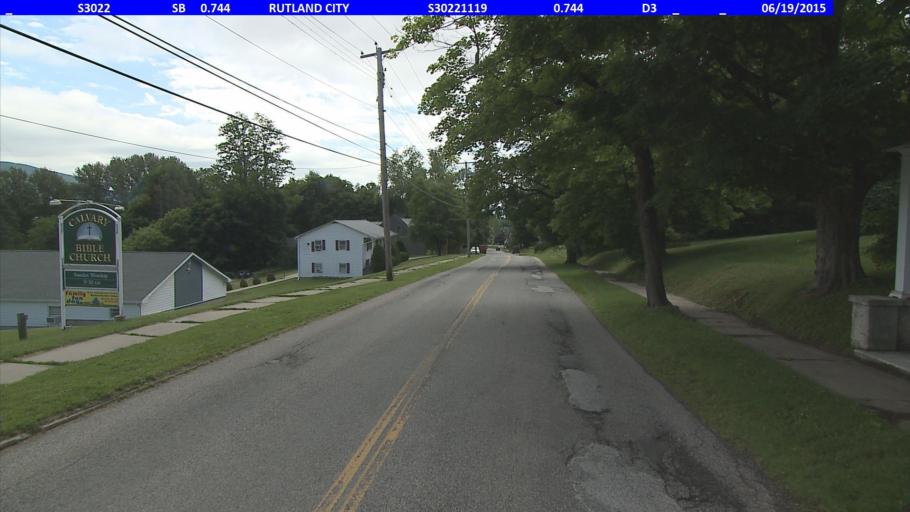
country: US
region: Vermont
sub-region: Rutland County
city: Rutland
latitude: 43.6194
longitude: -72.9847
